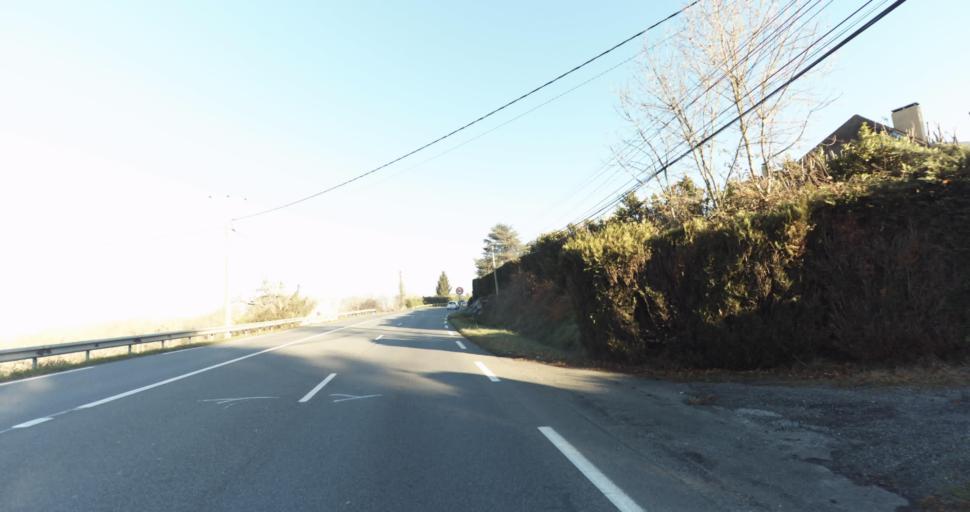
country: FR
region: Aquitaine
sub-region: Departement des Pyrenees-Atlantiques
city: Morlaas
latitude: 43.3334
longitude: -0.2782
